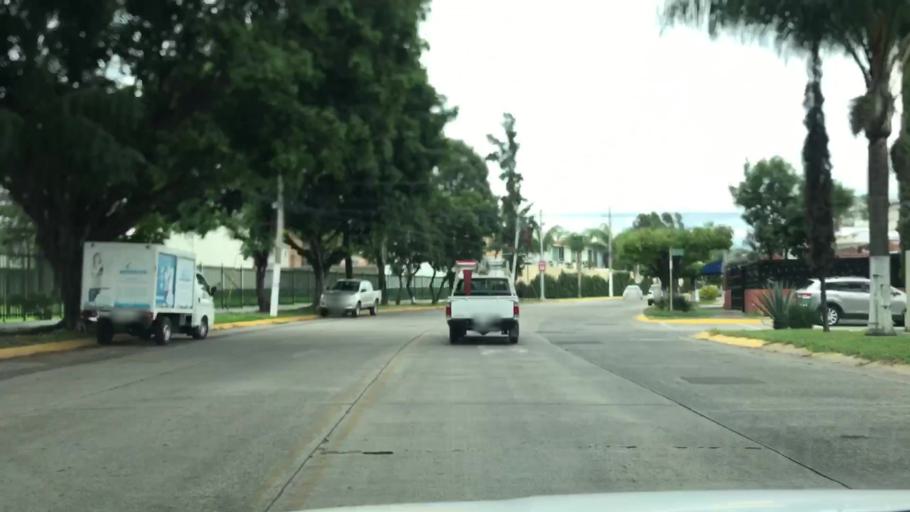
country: MX
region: Jalisco
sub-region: Tlajomulco de Zuniga
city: Palomar
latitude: 20.6396
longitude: -103.4381
